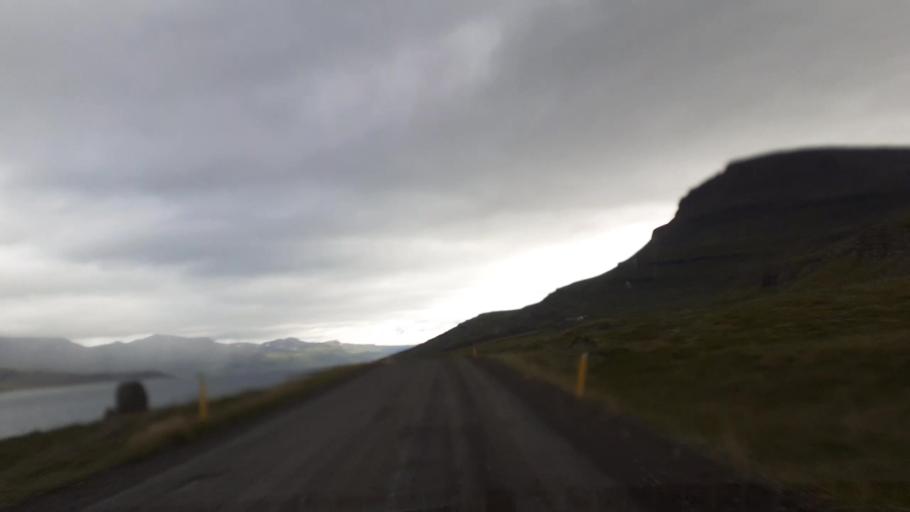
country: IS
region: East
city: Reydarfjoerdur
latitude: 65.0129
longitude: -14.1642
